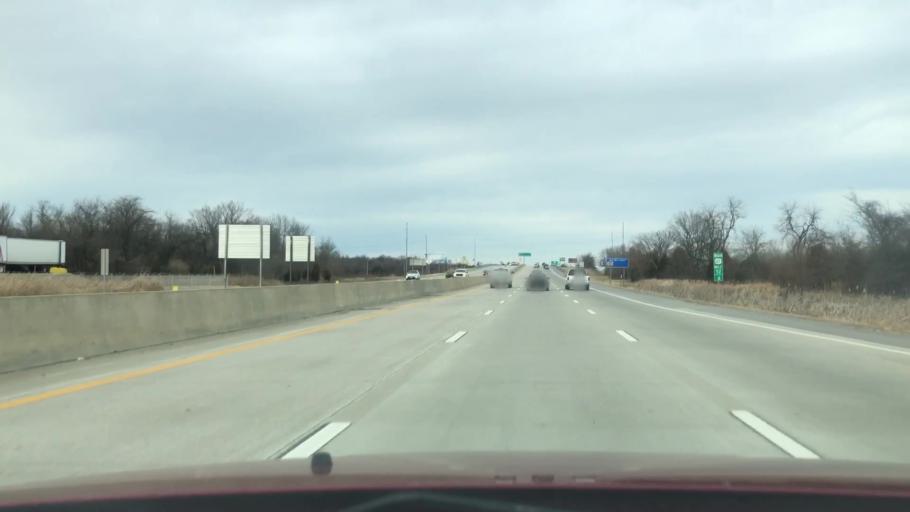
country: US
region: Missouri
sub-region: Greene County
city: Springfield
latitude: 37.2285
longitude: -93.2251
